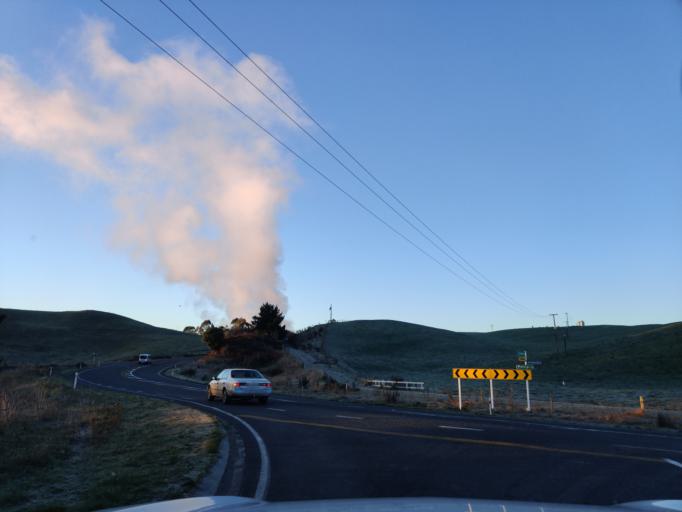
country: NZ
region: Waikato
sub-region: Taupo District
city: Taupo
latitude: -38.6227
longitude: 176.0366
